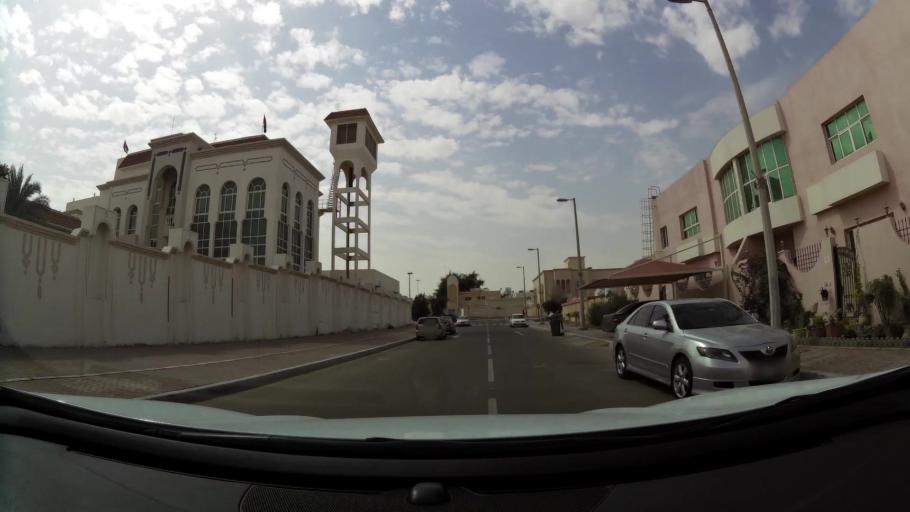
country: AE
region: Abu Dhabi
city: Abu Dhabi
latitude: 24.3071
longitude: 54.6146
